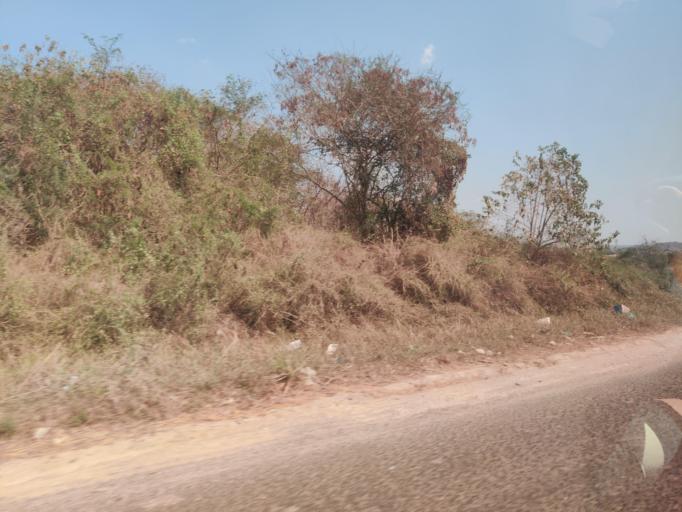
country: CO
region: Bolivar
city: Turbana
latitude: 10.2760
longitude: -75.5213
